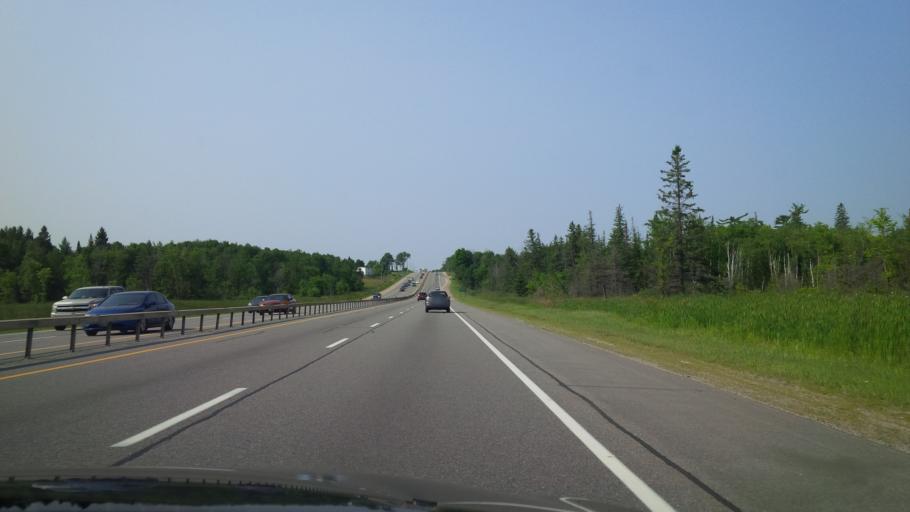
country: CA
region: Ontario
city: Orillia
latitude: 44.5397
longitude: -79.4562
